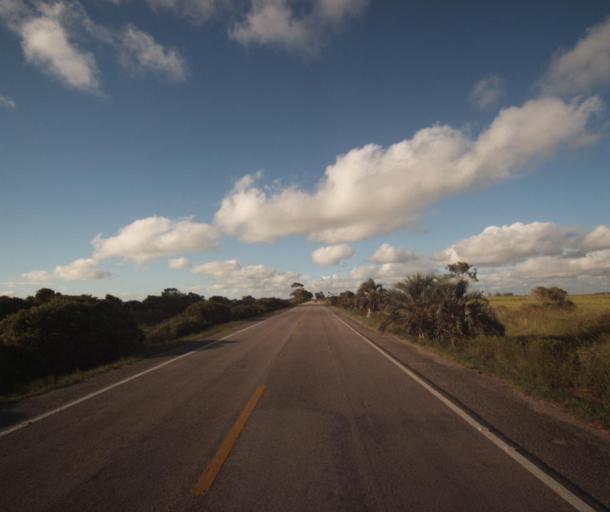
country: BR
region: Rio Grande do Sul
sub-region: Arroio Grande
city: Arroio Grande
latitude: -32.4865
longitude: -52.5793
